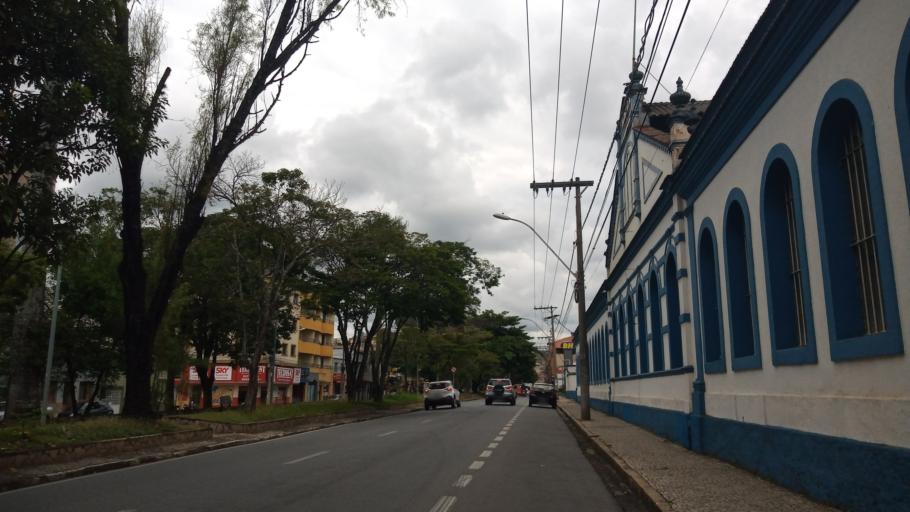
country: BR
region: Minas Gerais
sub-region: Sao Joao Del Rei
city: Sao Joao del Rei
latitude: -21.1268
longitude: -44.2493
